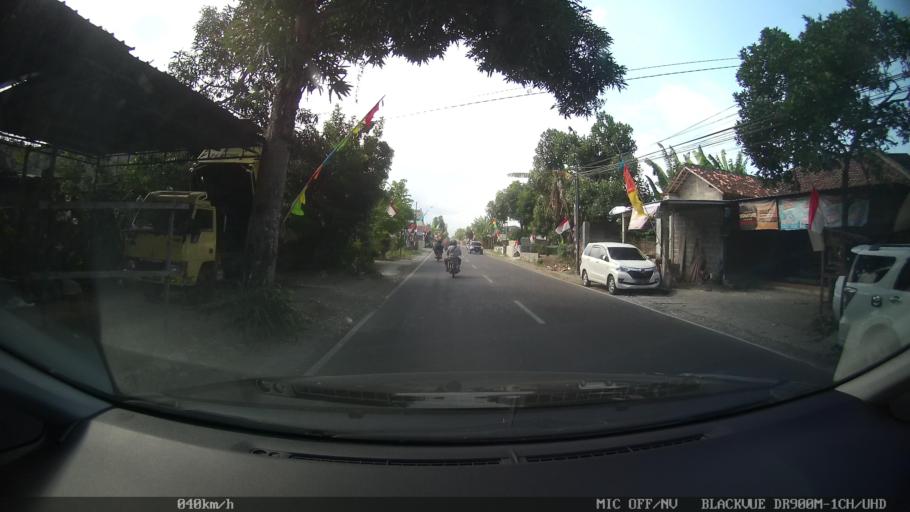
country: ID
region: Daerah Istimewa Yogyakarta
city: Sewon
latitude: -7.8620
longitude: 110.3894
